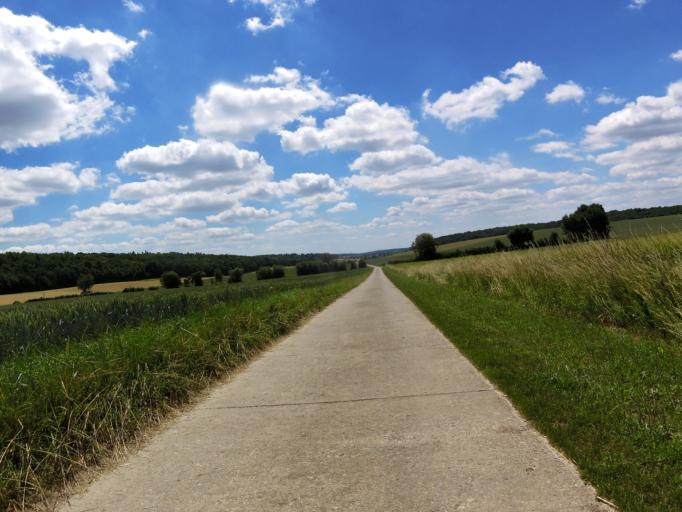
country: DE
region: Bavaria
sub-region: Regierungsbezirk Unterfranken
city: Kist
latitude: 49.7369
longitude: 9.8483
